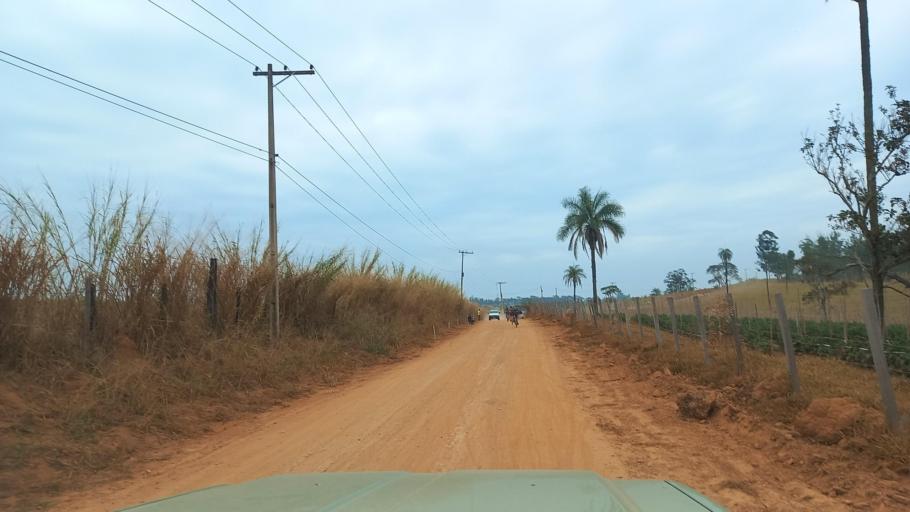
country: BR
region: Sao Paulo
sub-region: Moji-Guacu
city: Mogi-Gaucu
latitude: -22.3123
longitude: -46.8383
